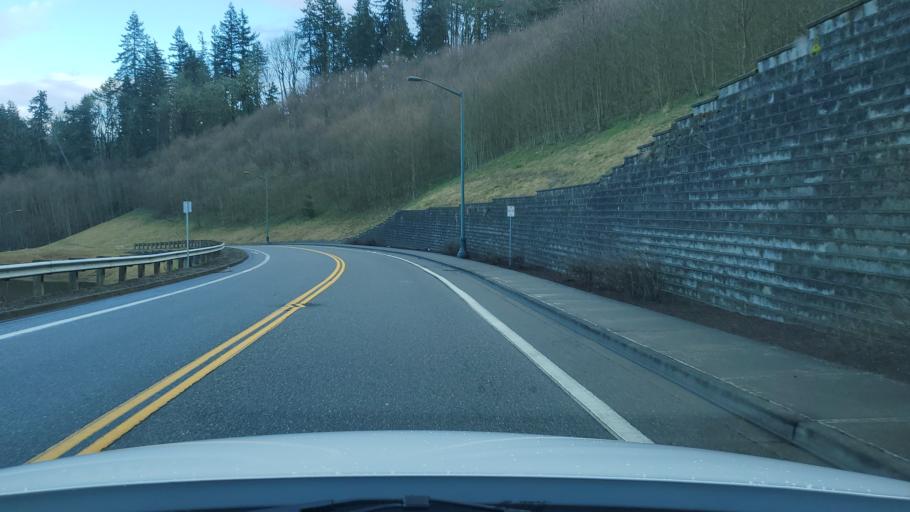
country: US
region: Washington
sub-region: Skagit County
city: Big Lake
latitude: 48.4293
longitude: -122.2713
